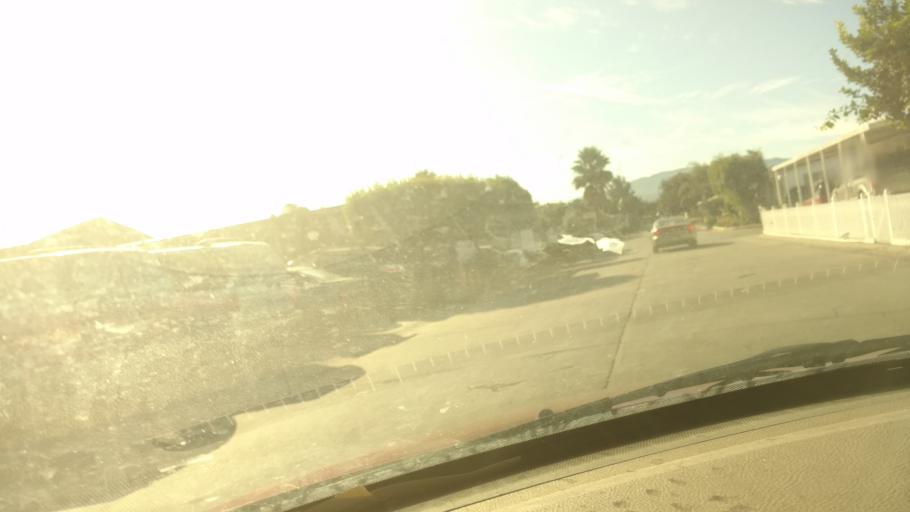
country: US
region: California
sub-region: San Benito County
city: Hollister
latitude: 36.8516
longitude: -121.4205
